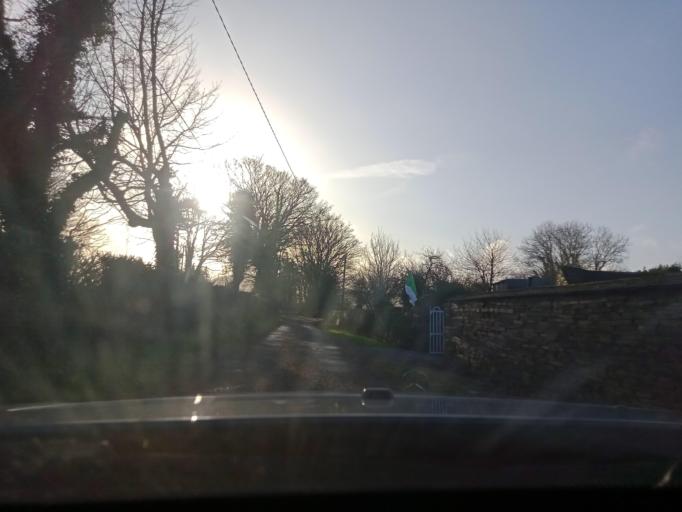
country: IE
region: Munster
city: Carrick-on-Suir
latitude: 52.4369
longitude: -7.4168
